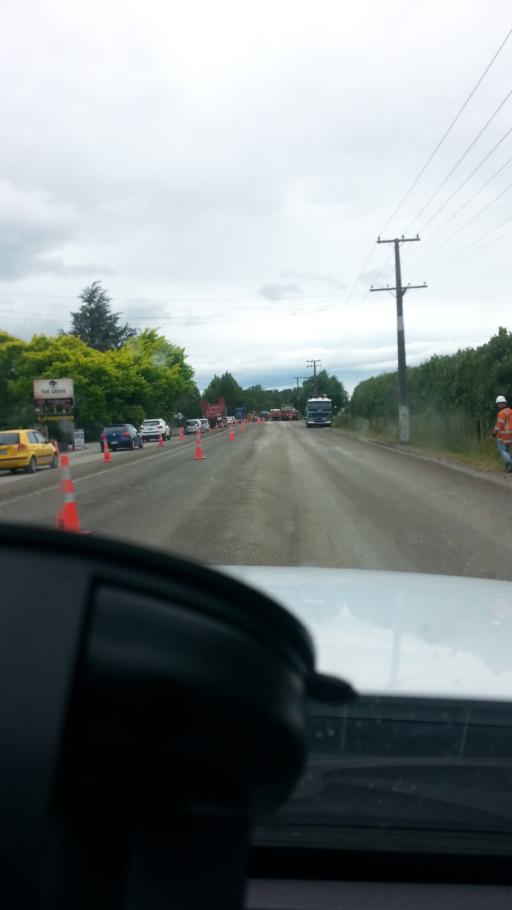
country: NZ
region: Wellington
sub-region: Masterton District
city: Masterton
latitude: -41.0709
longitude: 175.4710
